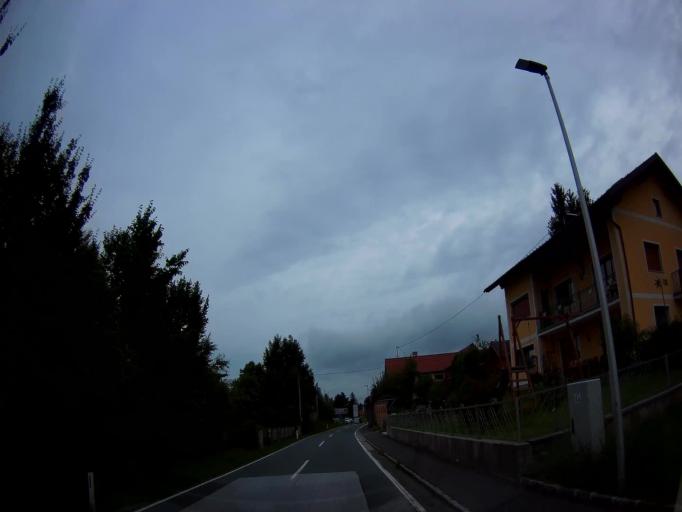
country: AT
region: Salzburg
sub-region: Politischer Bezirk Salzburg-Umgebung
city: Mattsee
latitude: 48.0810
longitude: 13.1462
